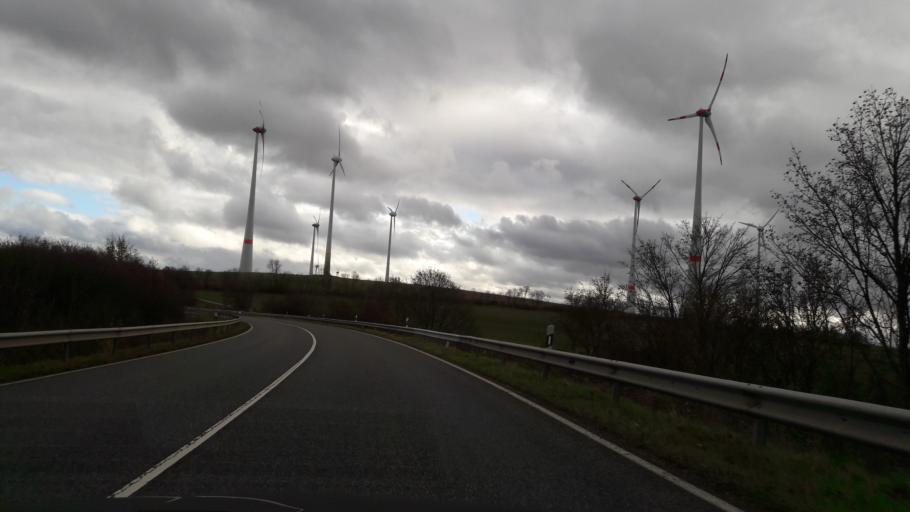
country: DE
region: Rheinland-Pfalz
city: Fell
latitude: 49.7576
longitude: 6.7658
